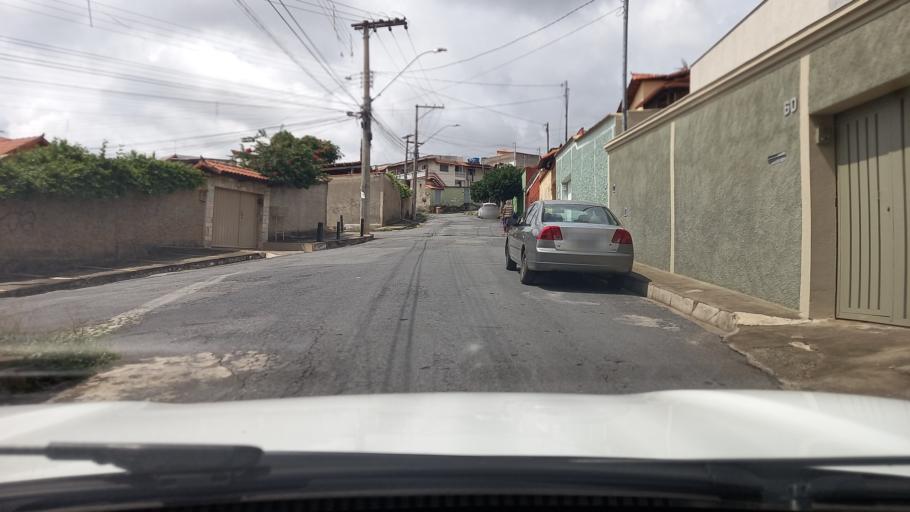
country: BR
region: Minas Gerais
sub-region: Contagem
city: Contagem
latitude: -19.9018
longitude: -44.0261
